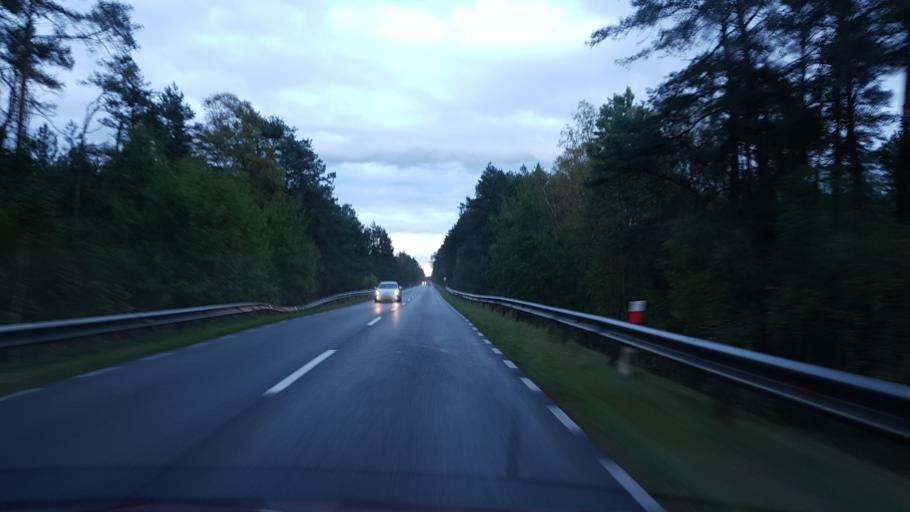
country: PL
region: Greater Poland Voivodeship
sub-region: Powiat pilski
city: Smilowo
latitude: 53.2081
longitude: 16.8496
